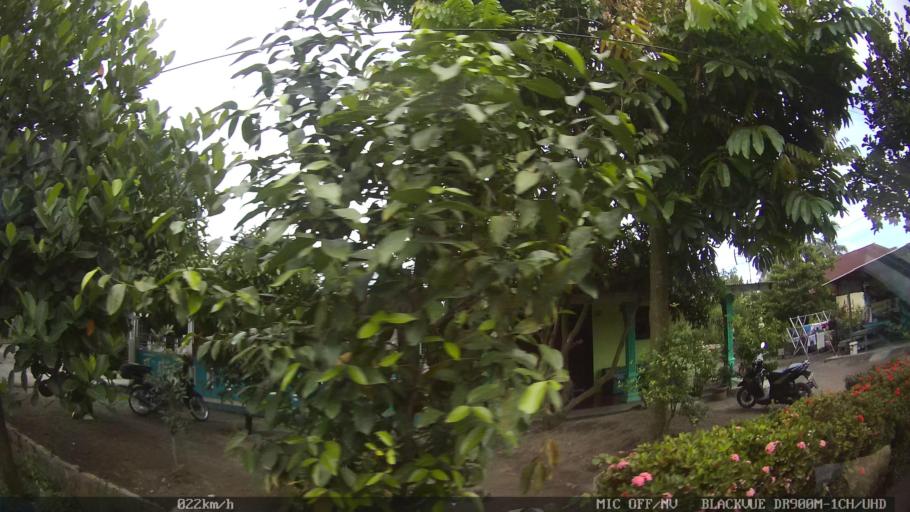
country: ID
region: North Sumatra
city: Sunggal
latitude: 3.5951
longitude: 98.5659
